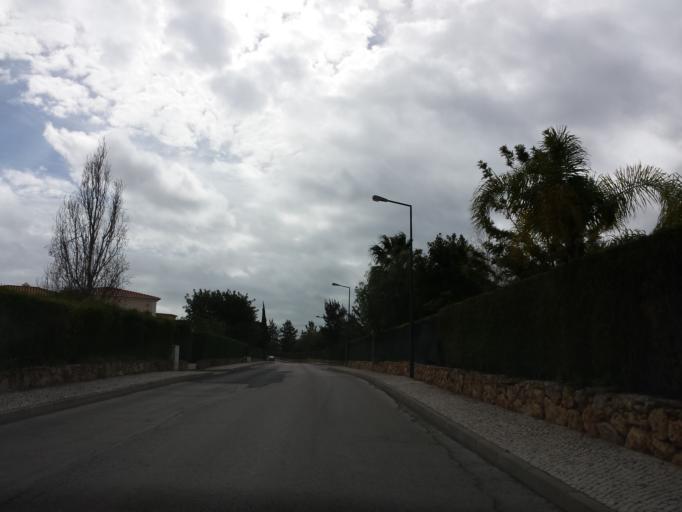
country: PT
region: Faro
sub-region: Lagoa
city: Estombar
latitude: 37.1295
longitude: -8.4855
